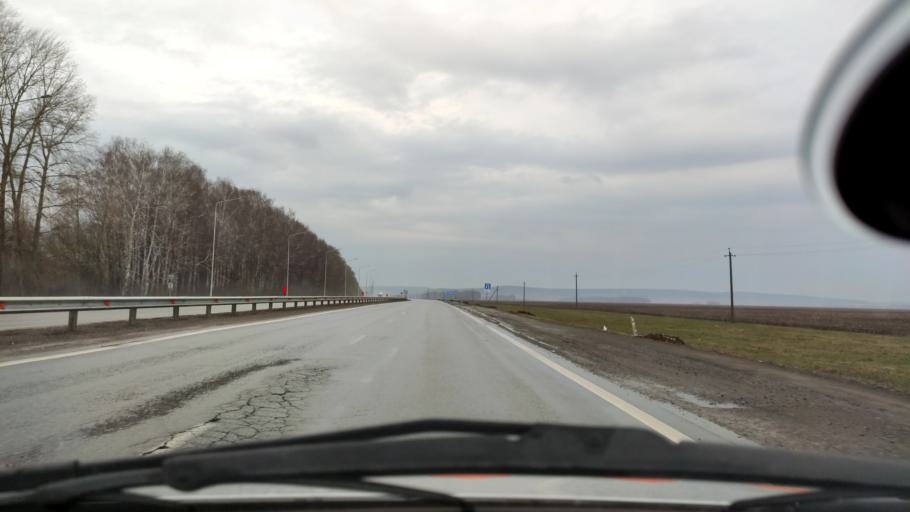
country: RU
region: Bashkortostan
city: Sterlitamak
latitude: 53.7722
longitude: 55.9439
